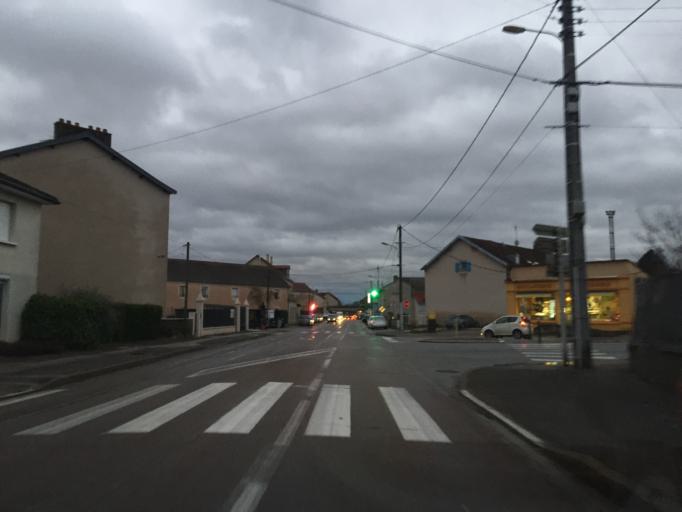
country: FR
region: Franche-Comte
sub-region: Departement du Jura
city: Dole
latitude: 47.1000
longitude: 5.4917
